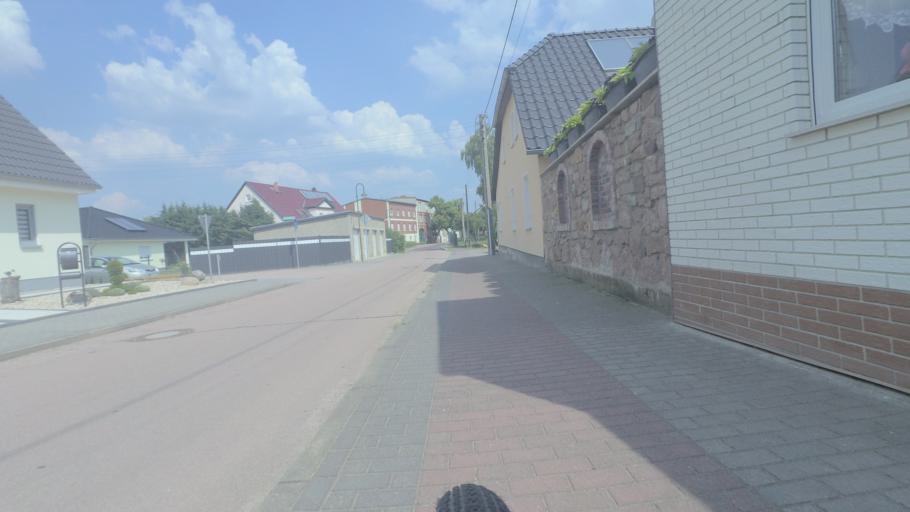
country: DE
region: Saxony-Anhalt
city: Koethen
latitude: 51.7618
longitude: 11.9317
